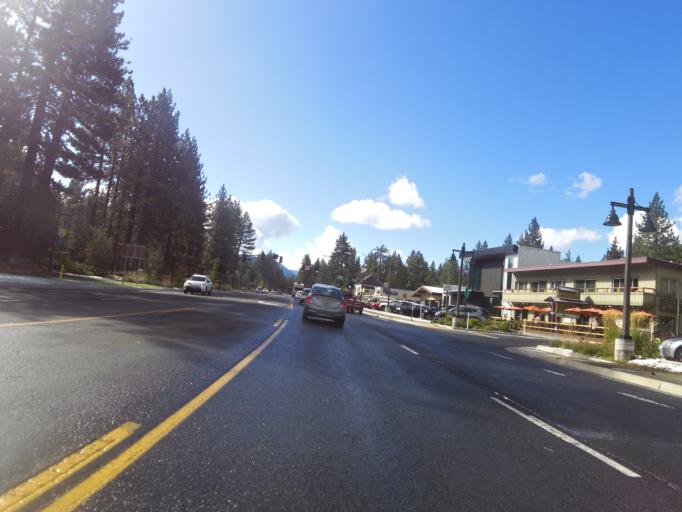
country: US
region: California
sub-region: El Dorado County
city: South Lake Tahoe
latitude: 38.9425
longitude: -119.9772
